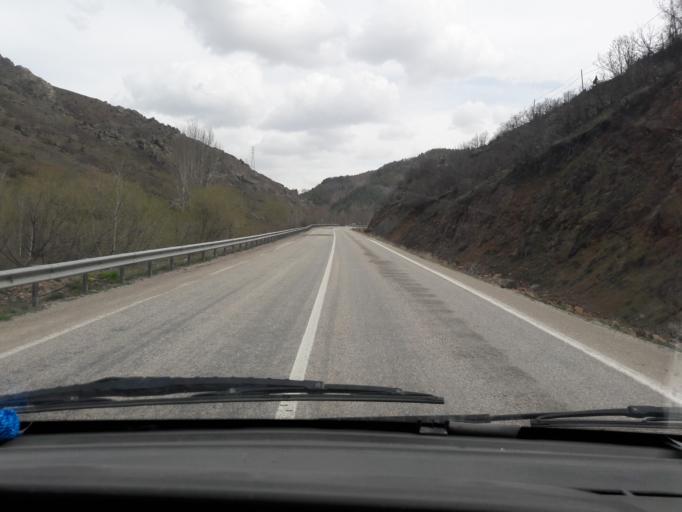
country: TR
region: Gumushane
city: Gumushkhane
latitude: 40.2968
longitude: 39.4745
